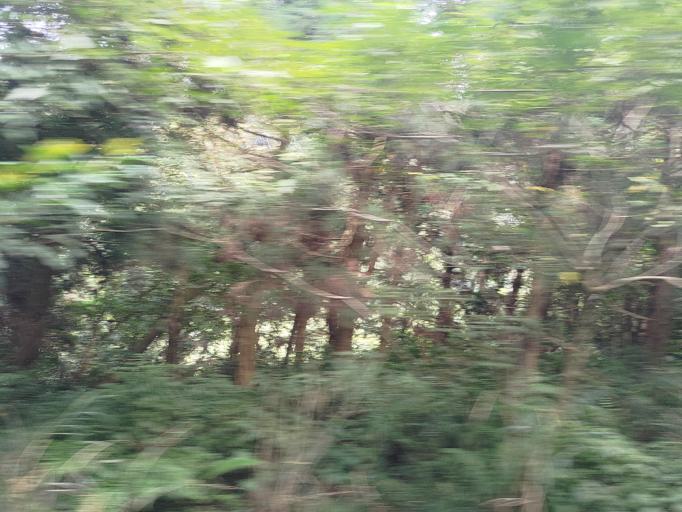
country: TW
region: Taiwan
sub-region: Hsinchu
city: Hsinchu
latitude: 24.6280
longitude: 121.0789
